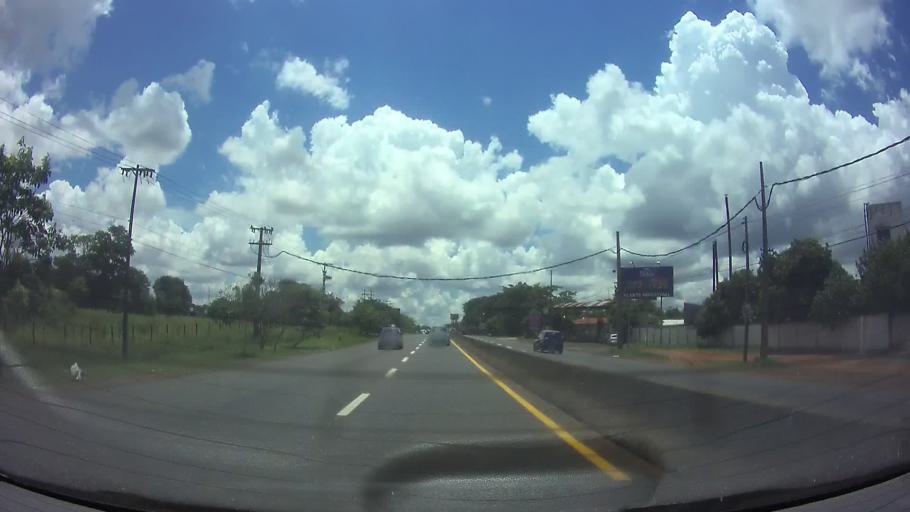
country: PY
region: Central
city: Itaugua
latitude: -25.3807
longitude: -57.3778
